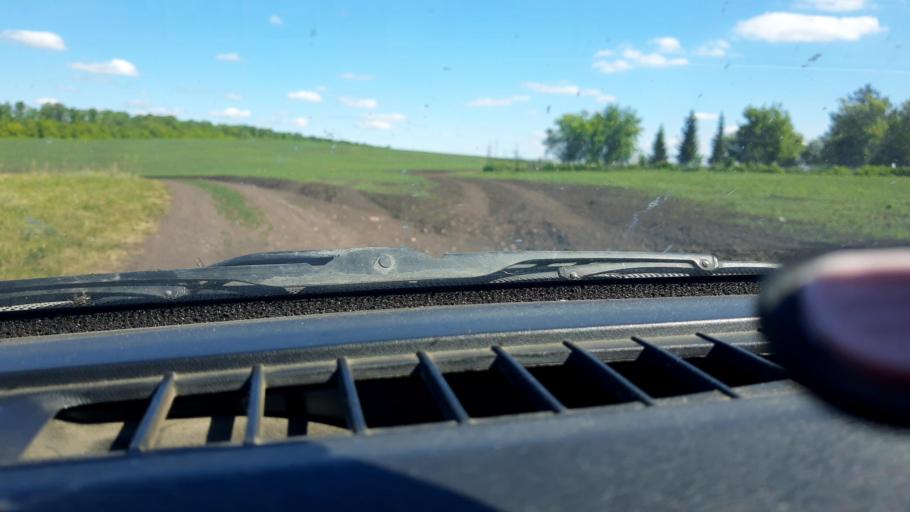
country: RU
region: Bashkortostan
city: Avdon
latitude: 54.6554
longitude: 55.7821
